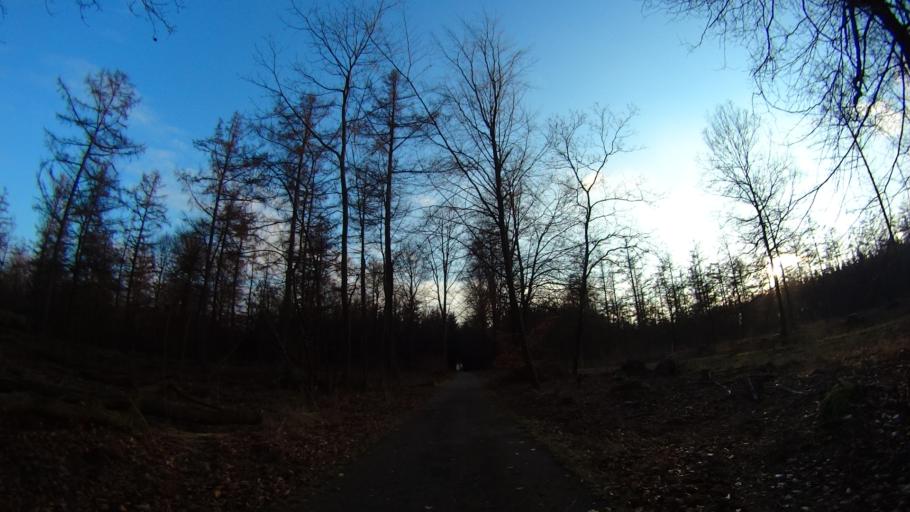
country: NL
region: Drenthe
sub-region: Gemeente Coevorden
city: Sleen
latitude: 52.8029
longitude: 6.7694
